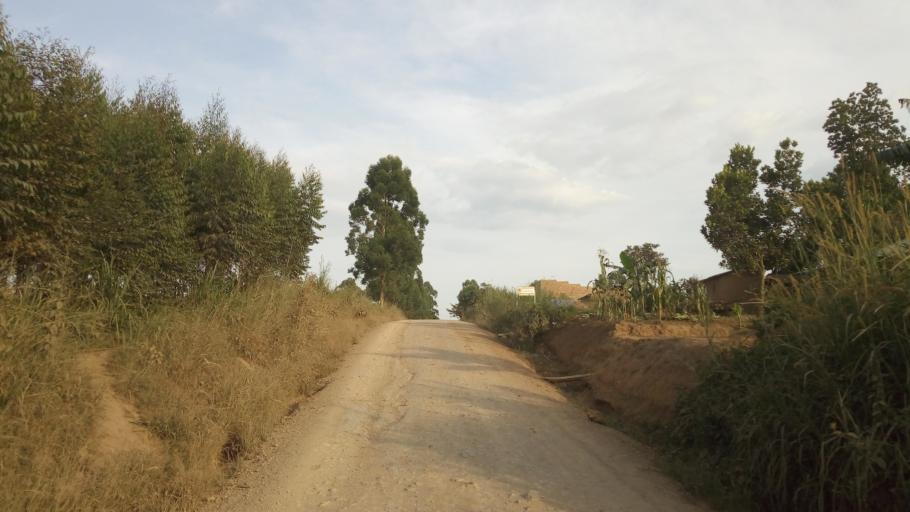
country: UG
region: Central Region
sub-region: Kiboga District
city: Kiboga
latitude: 0.7070
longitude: 31.7737
